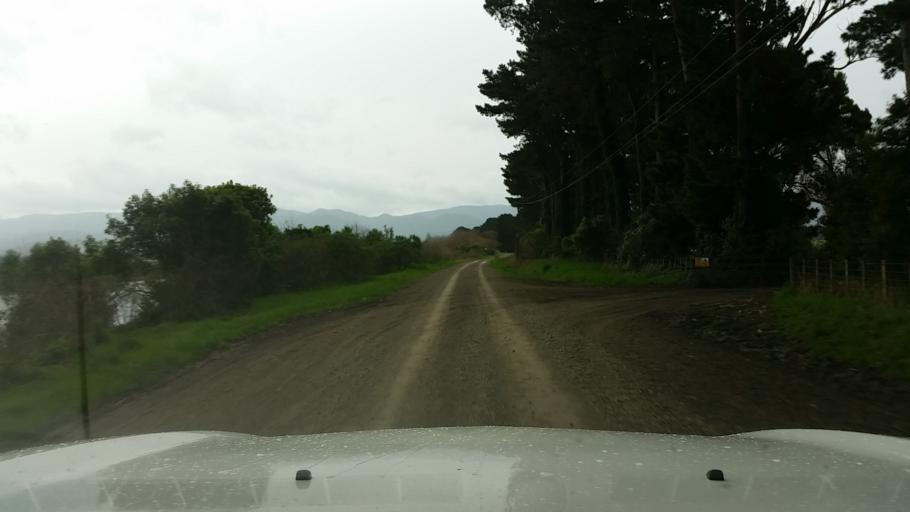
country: NZ
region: Wellington
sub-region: Upper Hutt City
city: Upper Hutt
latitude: -41.2938
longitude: 175.2260
